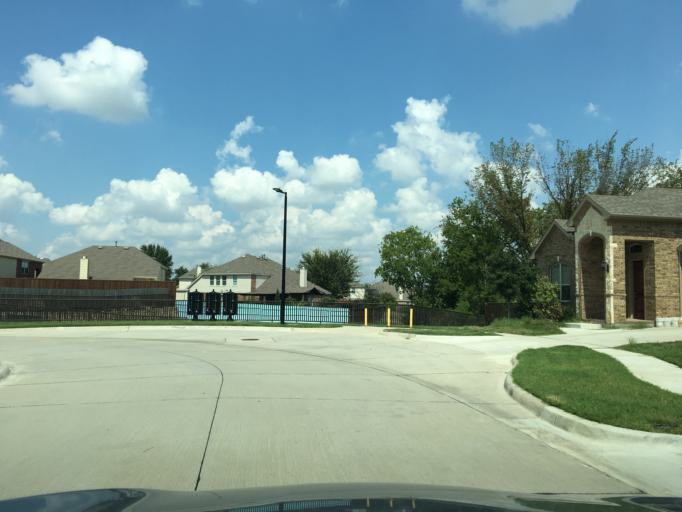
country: US
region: Texas
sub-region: Dallas County
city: Garland
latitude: 32.9496
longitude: -96.6419
